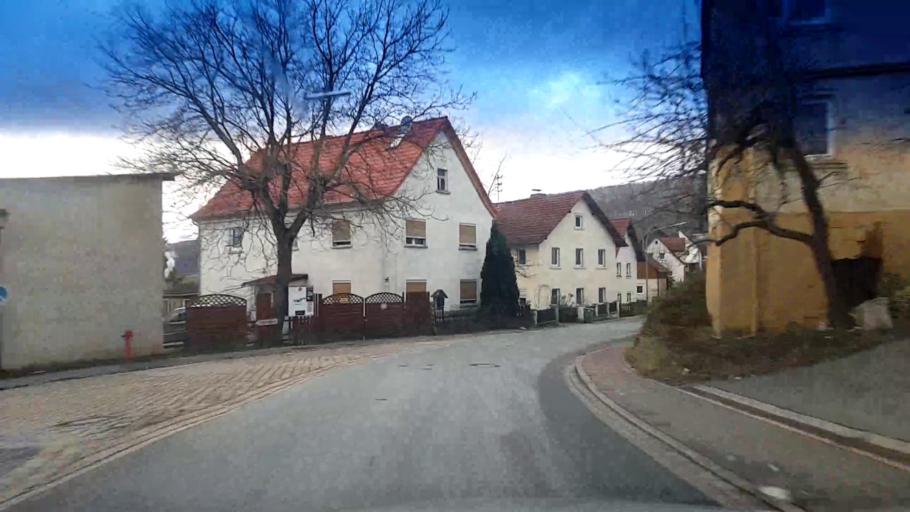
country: DE
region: Bavaria
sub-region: Upper Franconia
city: Litzendorf
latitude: 49.8740
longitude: 11.0673
